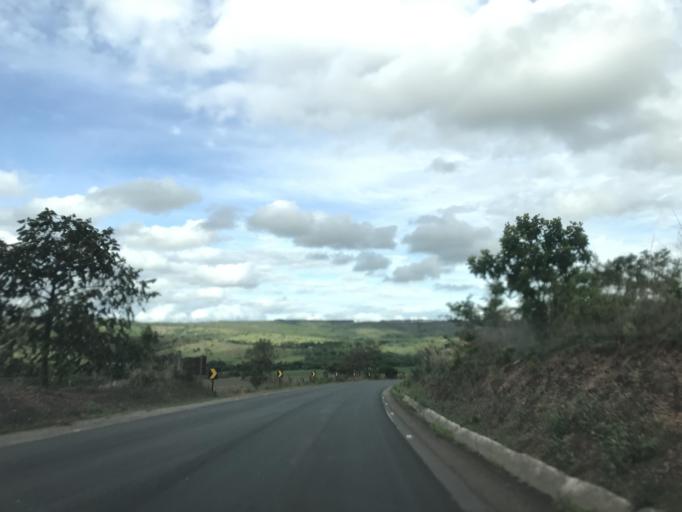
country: BR
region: Goias
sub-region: Vianopolis
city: Vianopolis
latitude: -16.9475
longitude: -48.5884
